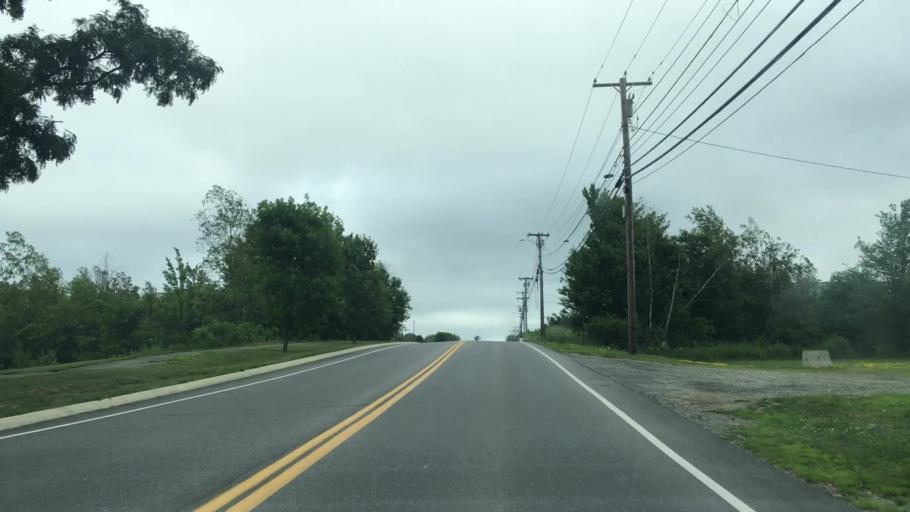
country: US
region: Maine
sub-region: Penobscot County
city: Brewer
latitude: 44.7794
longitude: -68.7633
